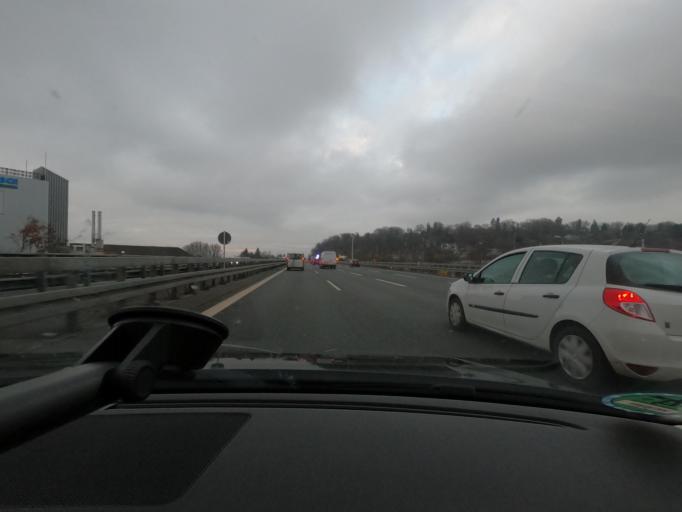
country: DE
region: Bavaria
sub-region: Regierungsbezirk Mittelfranken
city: Erlangen
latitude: 49.6046
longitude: 10.9985
